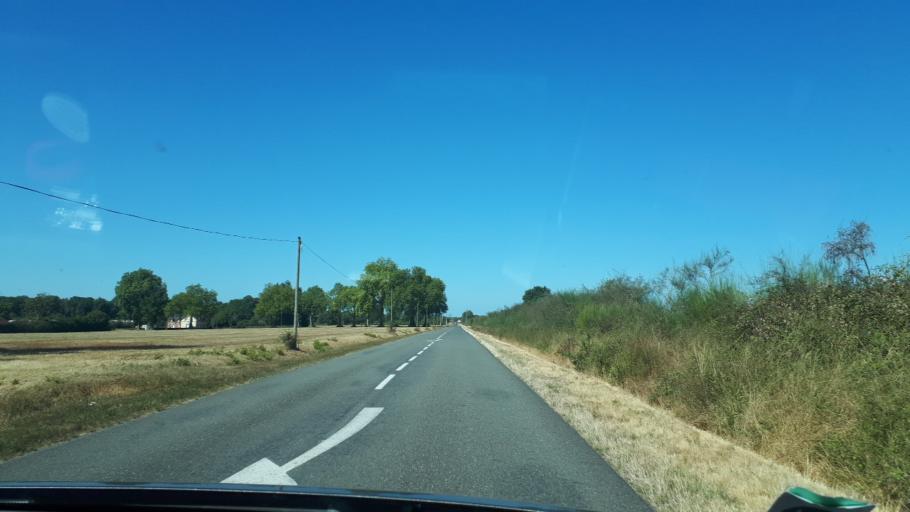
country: FR
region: Centre
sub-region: Departement du Loiret
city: Coullons
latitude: 47.6378
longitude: 2.4413
